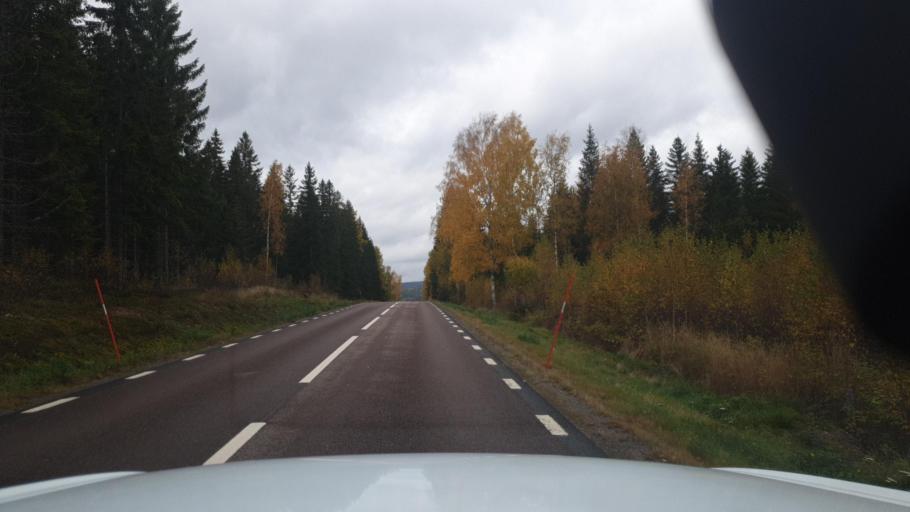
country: SE
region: Vaermland
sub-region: Sunne Kommun
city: Sunne
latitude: 59.8361
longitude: 12.9627
